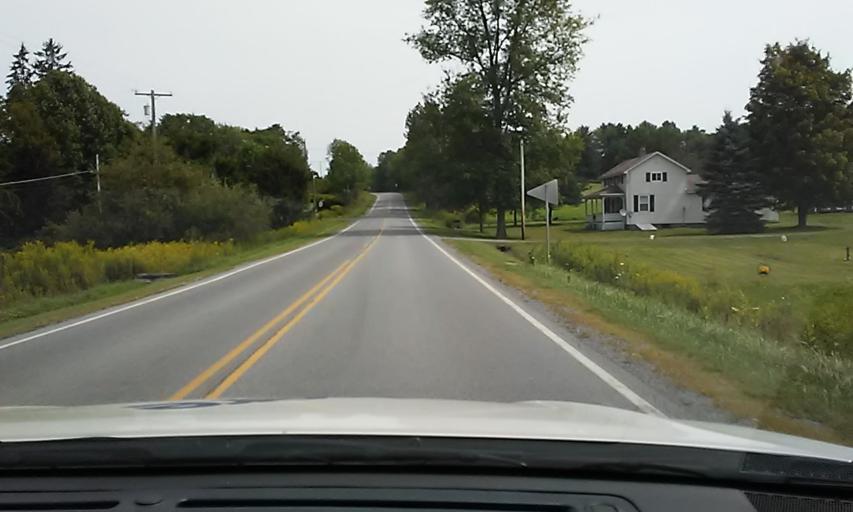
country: US
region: Pennsylvania
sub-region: Elk County
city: Saint Marys
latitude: 41.3473
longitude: -78.6159
